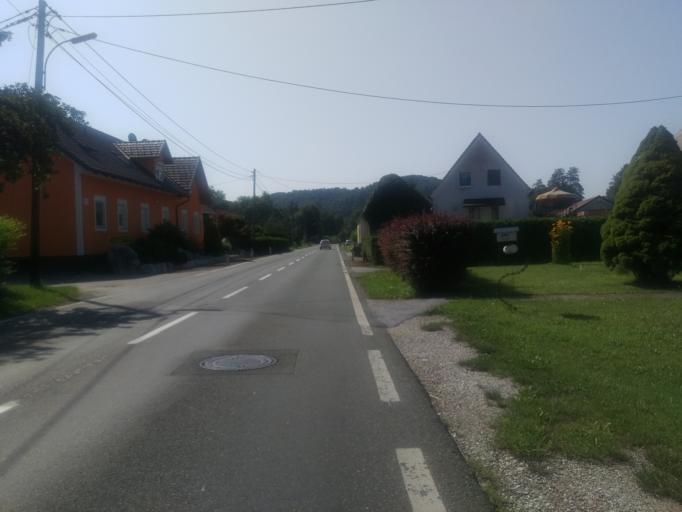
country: AT
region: Styria
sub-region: Politischer Bezirk Graz-Umgebung
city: Fernitz
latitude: 46.9584
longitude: 15.5066
